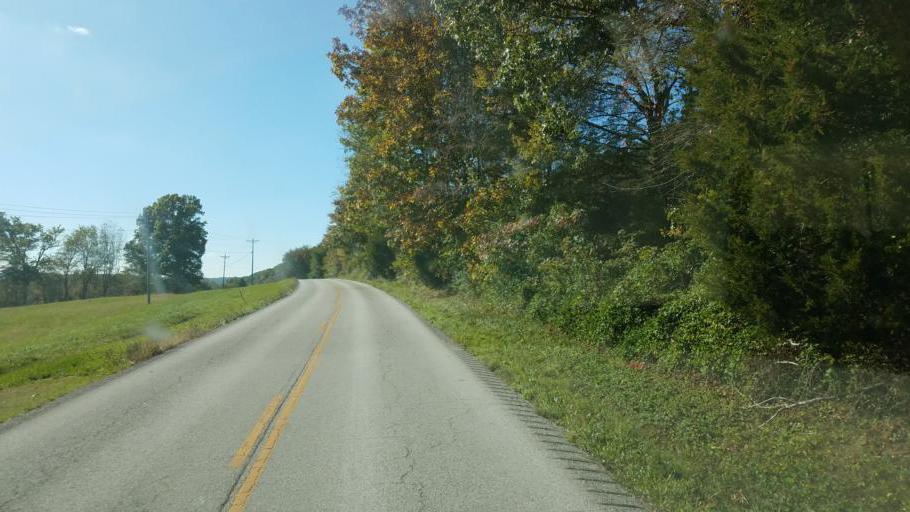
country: US
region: Kentucky
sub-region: Fleming County
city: Flemingsburg
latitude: 38.4687
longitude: -83.5533
